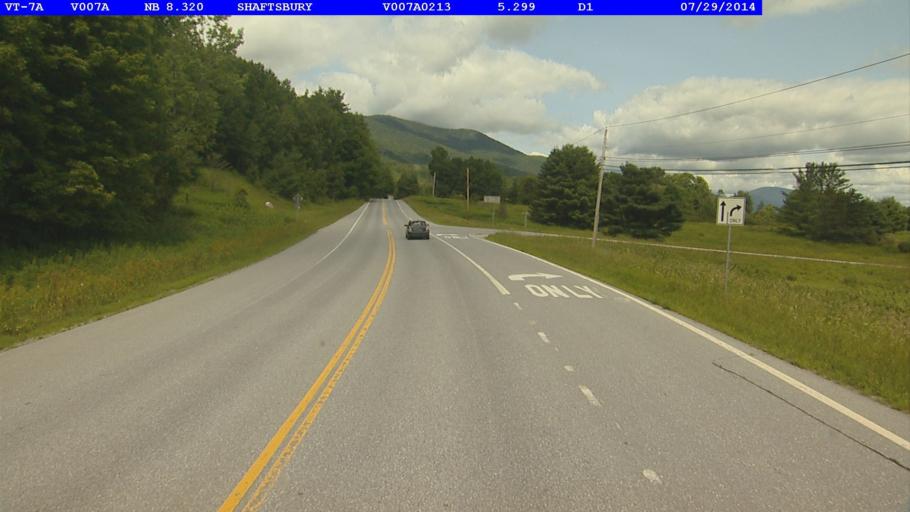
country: US
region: Vermont
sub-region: Bennington County
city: Arlington
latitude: 43.0065
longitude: -73.1945
